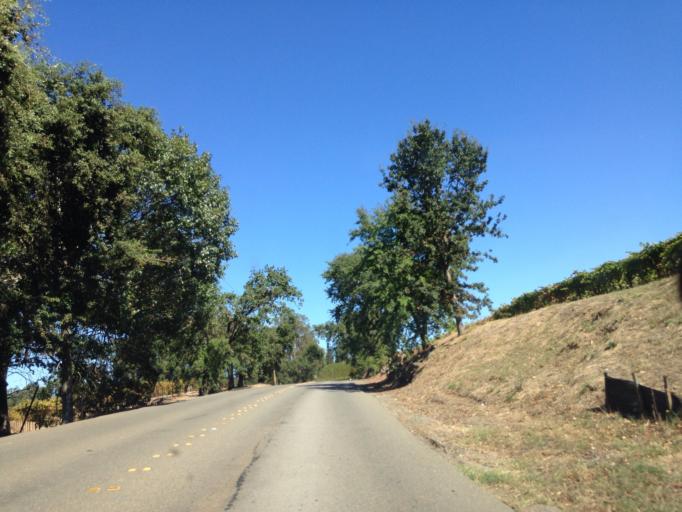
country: US
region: California
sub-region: Sonoma County
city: Windsor
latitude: 38.5589
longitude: -122.8461
